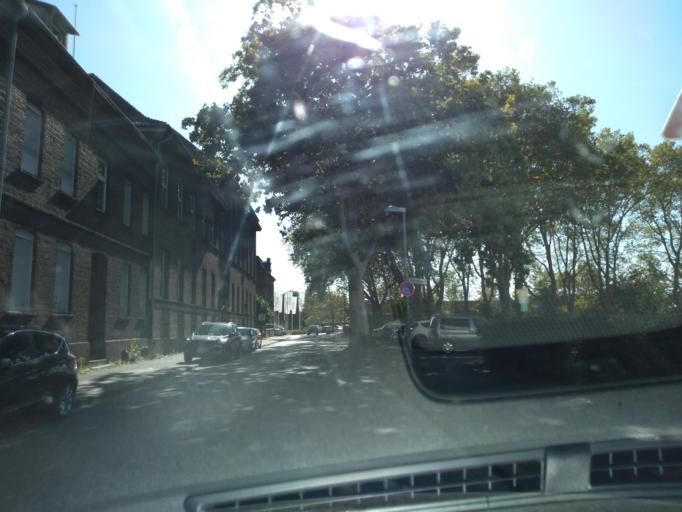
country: DE
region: North Rhine-Westphalia
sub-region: Regierungsbezirk Dusseldorf
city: Dinslaken
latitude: 51.5621
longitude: 6.7445
